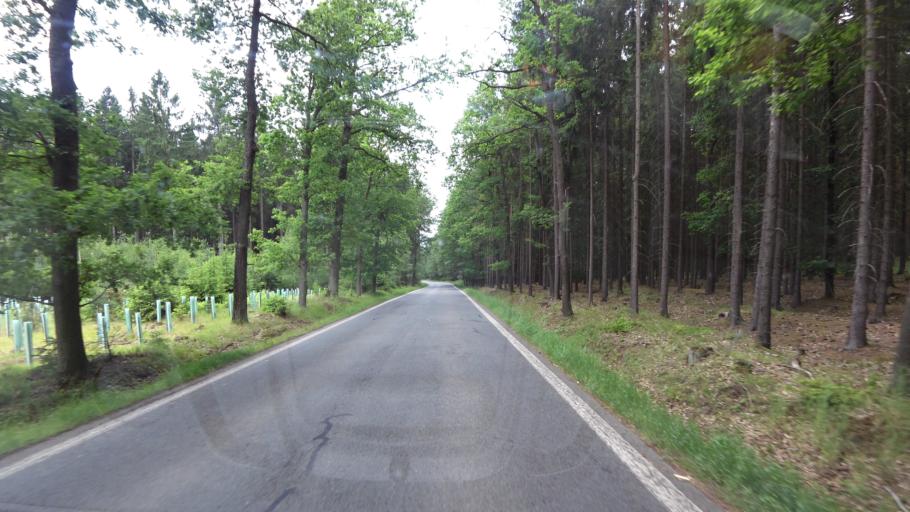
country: CZ
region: Plzensky
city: St'ahlavy
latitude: 49.6906
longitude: 13.5164
